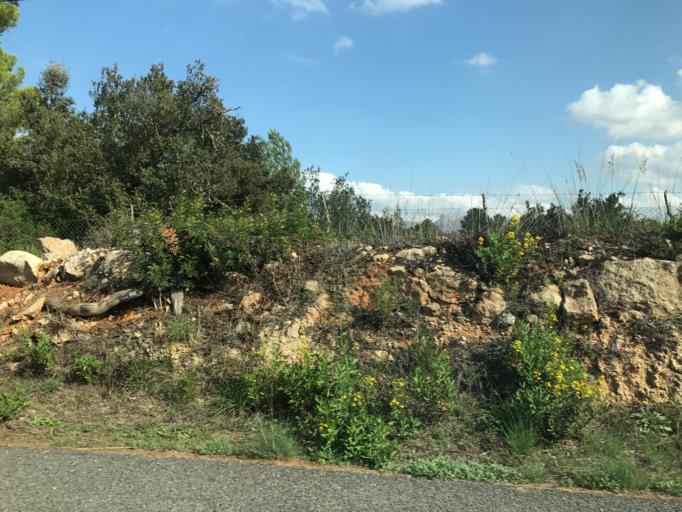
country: ES
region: Balearic Islands
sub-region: Illes Balears
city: Santa Margalida
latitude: 39.7264
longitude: 3.1992
